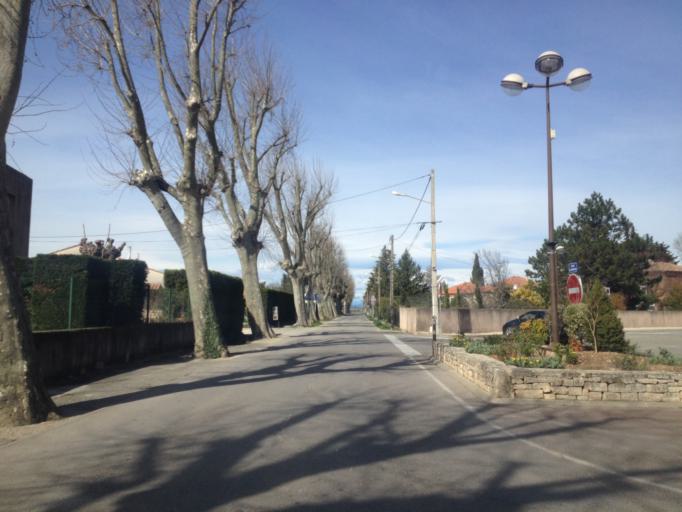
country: FR
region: Provence-Alpes-Cote d'Azur
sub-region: Departement du Vaucluse
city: Violes
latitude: 44.1625
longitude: 4.9508
